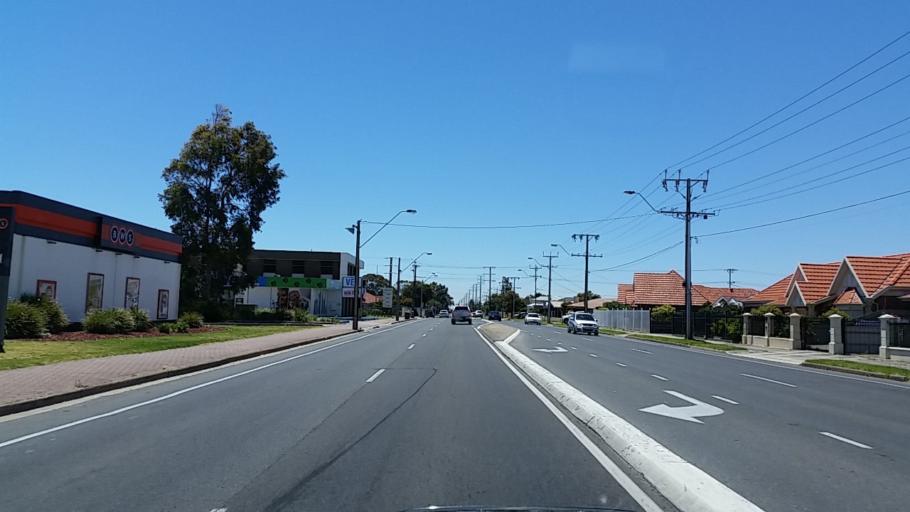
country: AU
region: South Australia
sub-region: Charles Sturt
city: Seaton
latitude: -34.9011
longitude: 138.5143
